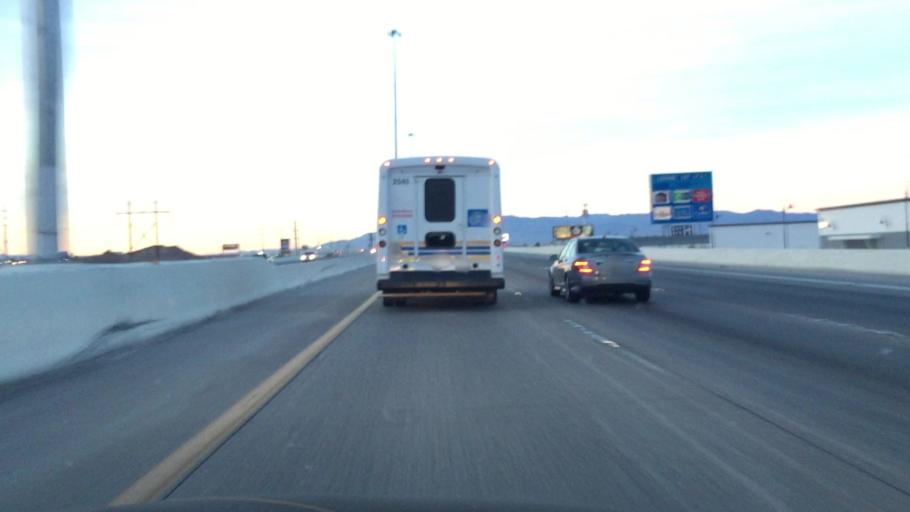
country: US
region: Nevada
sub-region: Clark County
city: Henderson
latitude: 36.0537
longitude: -115.0260
